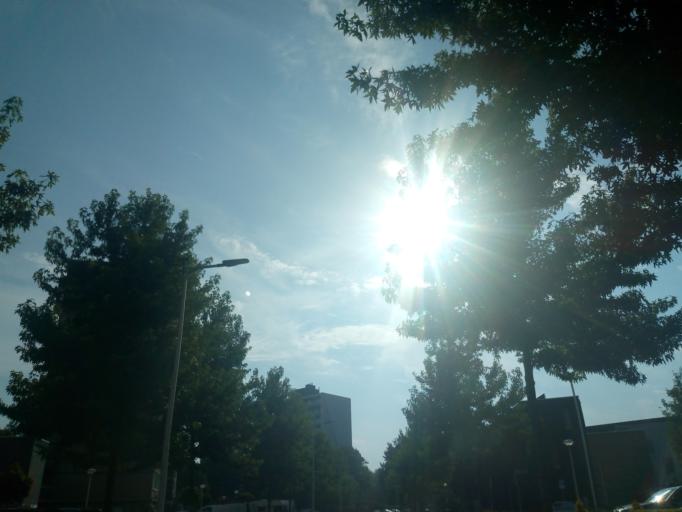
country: NL
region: South Holland
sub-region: Gemeente Alphen aan den Rijn
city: Alphen aan den Rijn
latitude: 52.1421
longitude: 4.6821
